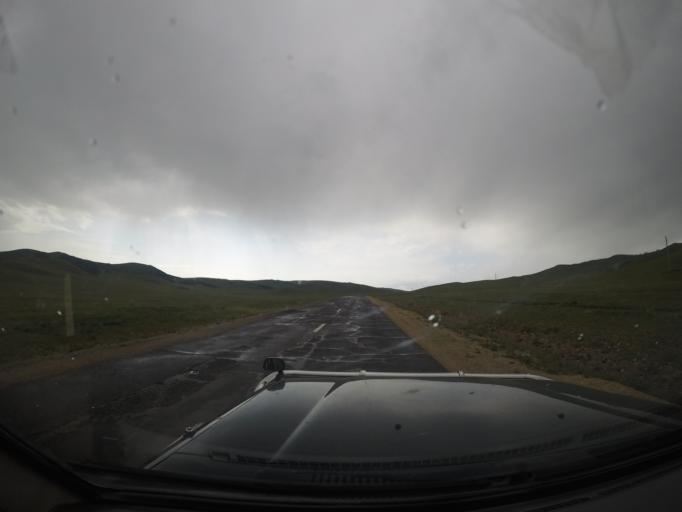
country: MN
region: Hentiy
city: Modot
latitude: 47.7686
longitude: 108.8784
